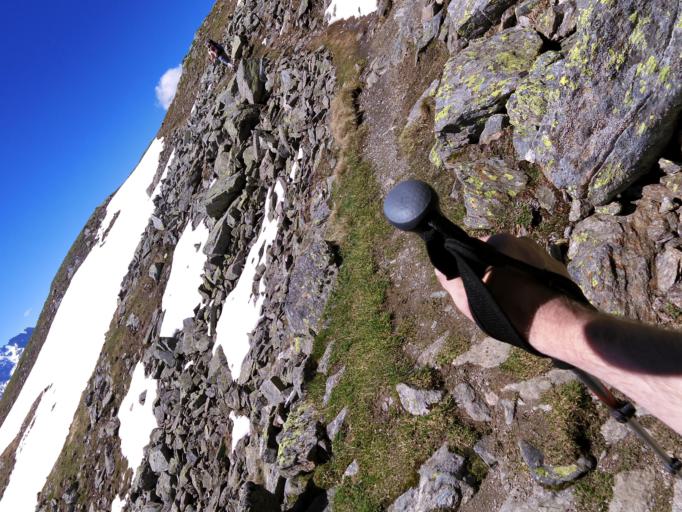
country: AT
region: Tyrol
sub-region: Politischer Bezirk Innsbruck Land
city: Neustift im Stubaital
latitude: 47.1393
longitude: 11.2602
